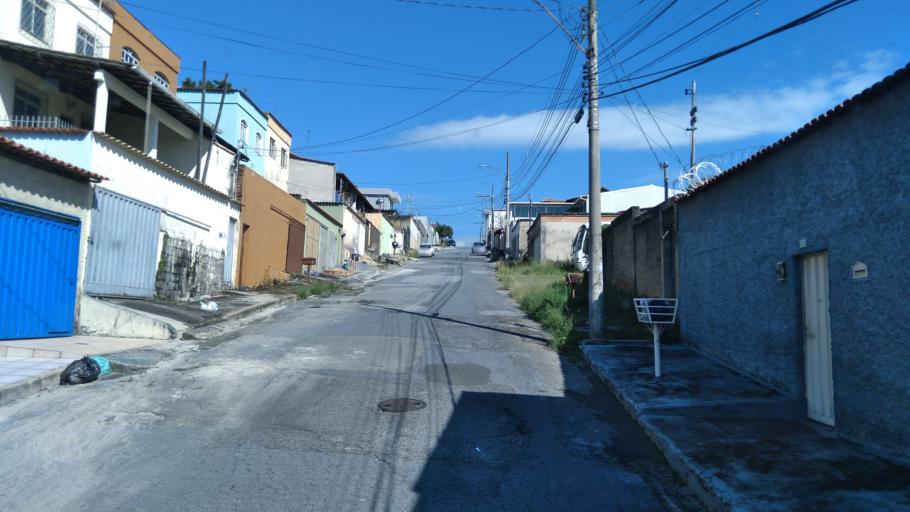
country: BR
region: Minas Gerais
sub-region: Santa Luzia
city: Santa Luzia
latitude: -19.8273
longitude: -43.8993
